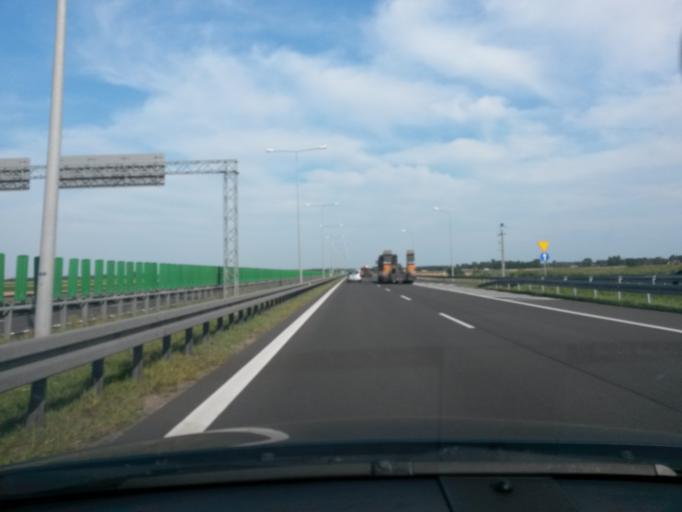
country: PL
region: Greater Poland Voivodeship
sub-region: Powiat slupecki
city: Strzalkowo
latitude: 52.2526
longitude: 17.8268
